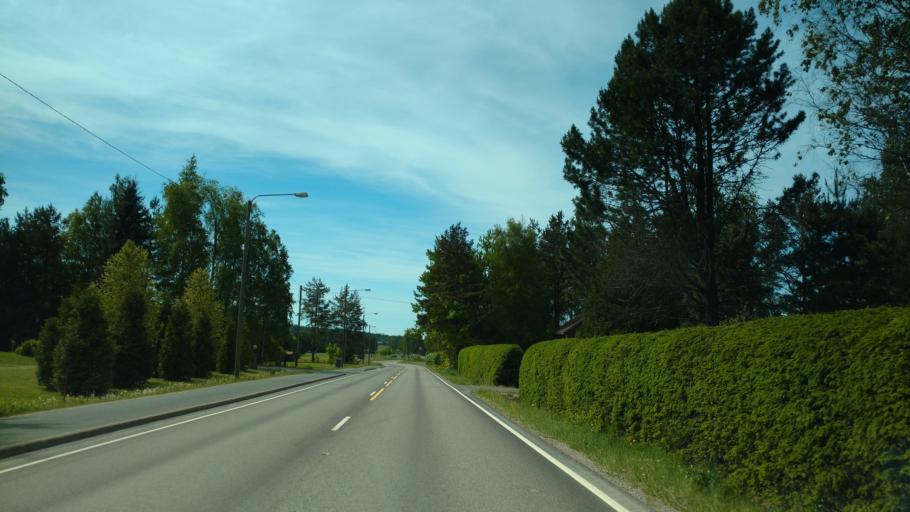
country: FI
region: Varsinais-Suomi
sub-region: Salo
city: Pertteli
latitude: 60.4223
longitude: 23.1973
